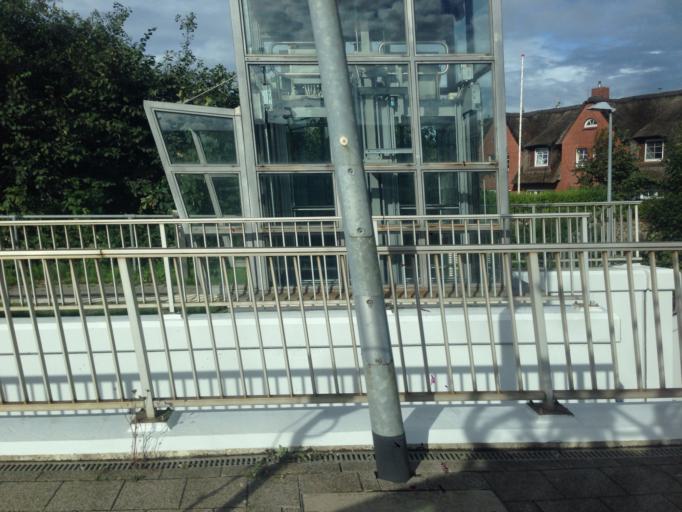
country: DE
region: Schleswig-Holstein
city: Keitum
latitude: 54.8883
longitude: 8.3705
